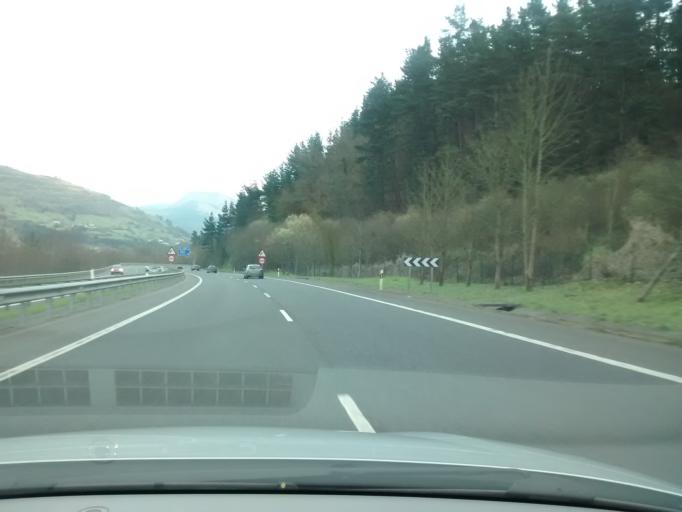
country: ES
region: Basque Country
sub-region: Bizkaia
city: Guenes
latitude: 43.2025
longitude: -3.0900
